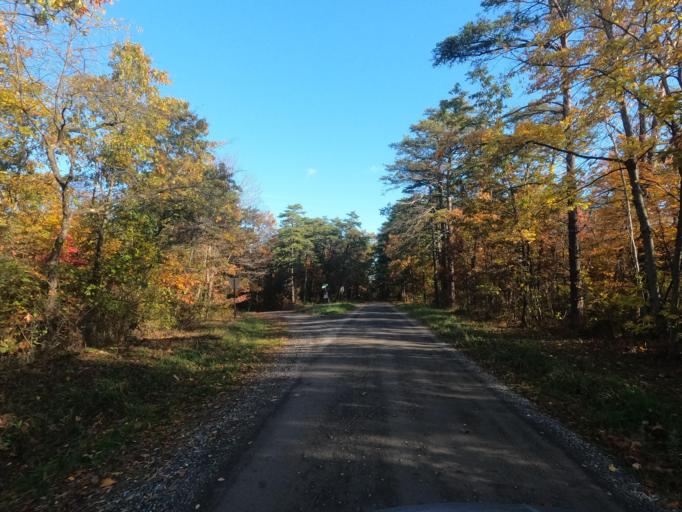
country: US
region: West Virginia
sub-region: Morgan County
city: Berkeley Springs
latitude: 39.6396
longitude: -78.4763
